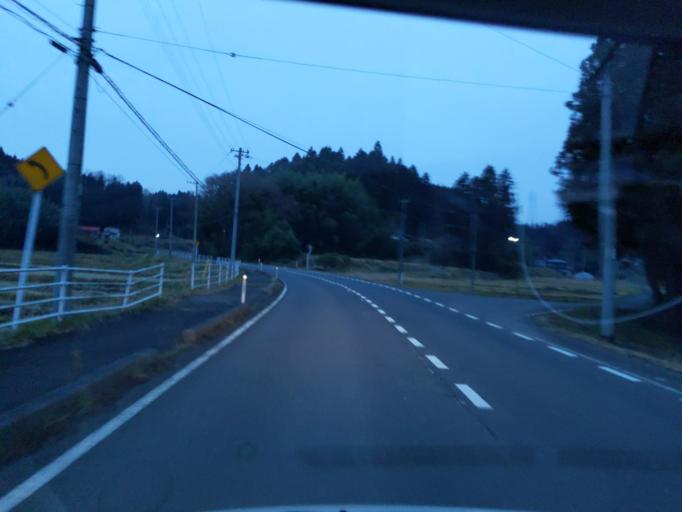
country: JP
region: Iwate
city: Ichinoseki
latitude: 38.8106
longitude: 141.1173
